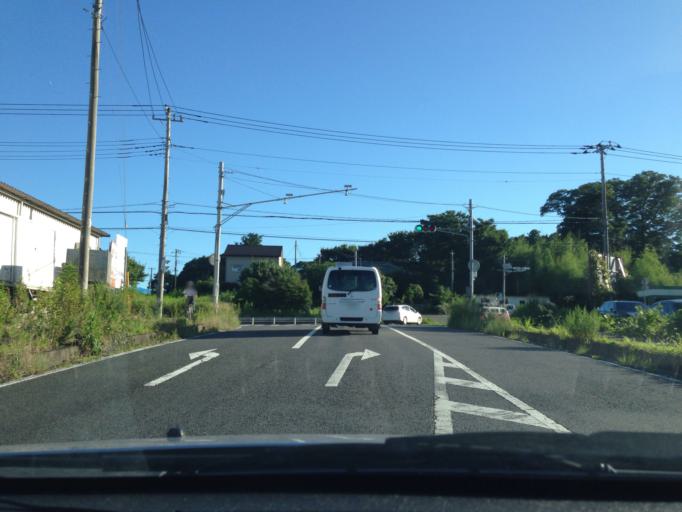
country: JP
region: Ibaraki
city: Naka
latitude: 36.0594
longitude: 140.1710
